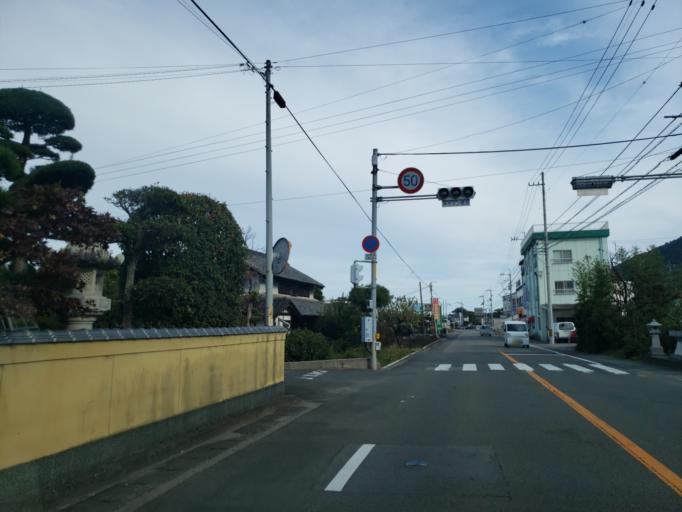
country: JP
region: Tokushima
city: Wakimachi
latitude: 34.0654
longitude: 134.1728
